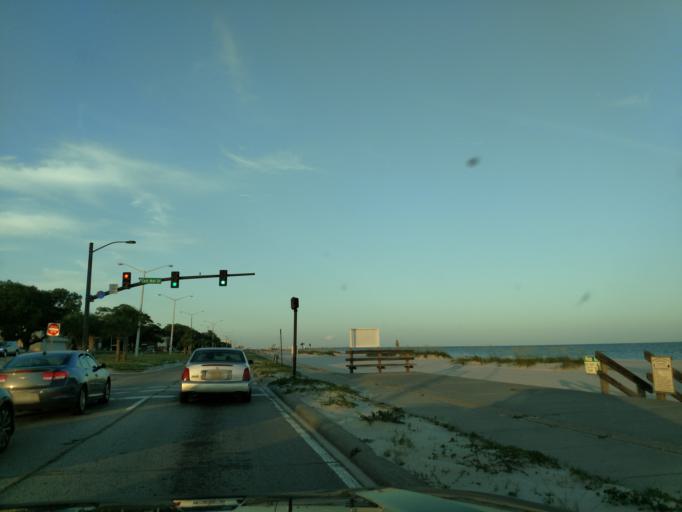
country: US
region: Mississippi
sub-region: Harrison County
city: Biloxi
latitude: 30.3893
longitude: -88.9895
